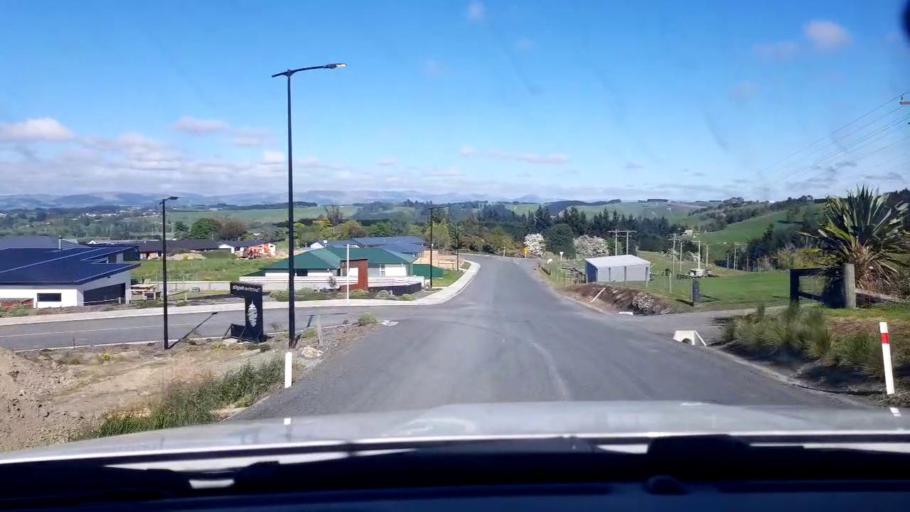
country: NZ
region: Otago
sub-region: Clutha District
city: Balclutha
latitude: -46.2238
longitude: 169.7488
